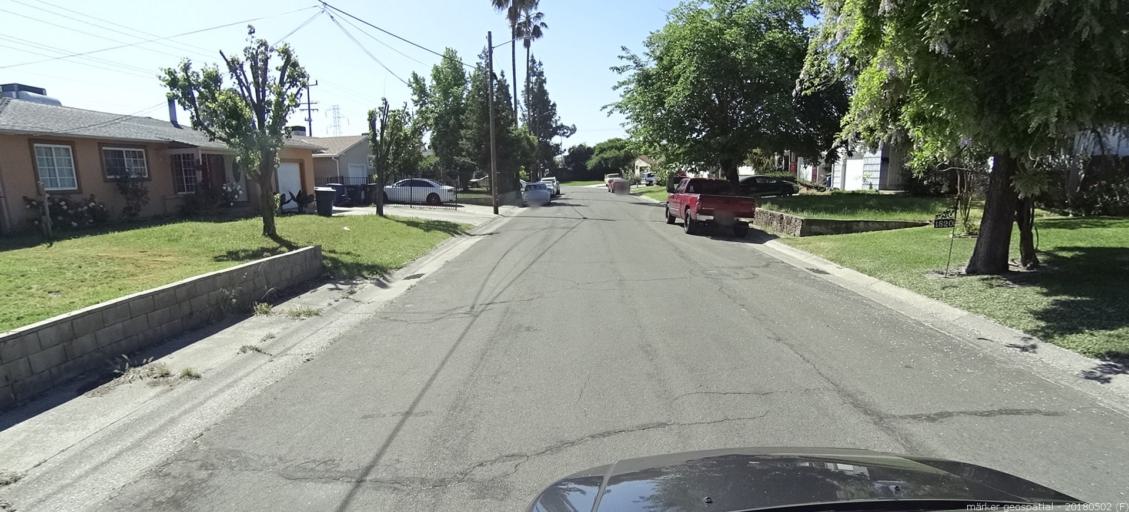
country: US
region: California
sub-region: Sacramento County
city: Arden-Arcade
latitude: 38.6024
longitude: -121.4249
